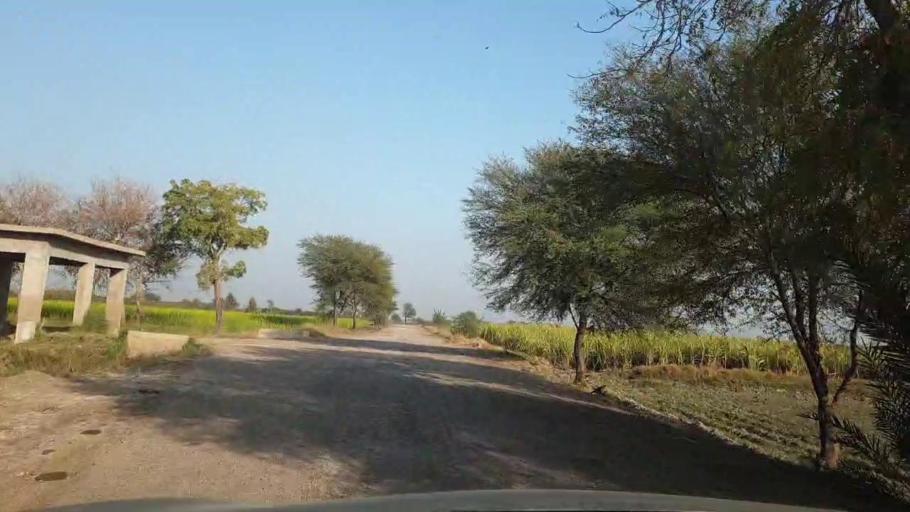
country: PK
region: Sindh
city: Tando Allahyar
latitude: 25.5864
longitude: 68.6738
